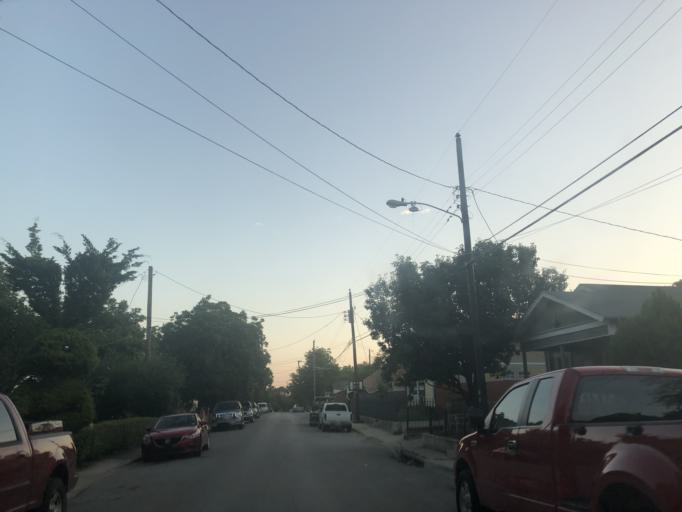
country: US
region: Texas
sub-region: Dallas County
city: Dallas
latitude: 32.7505
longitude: -96.8202
